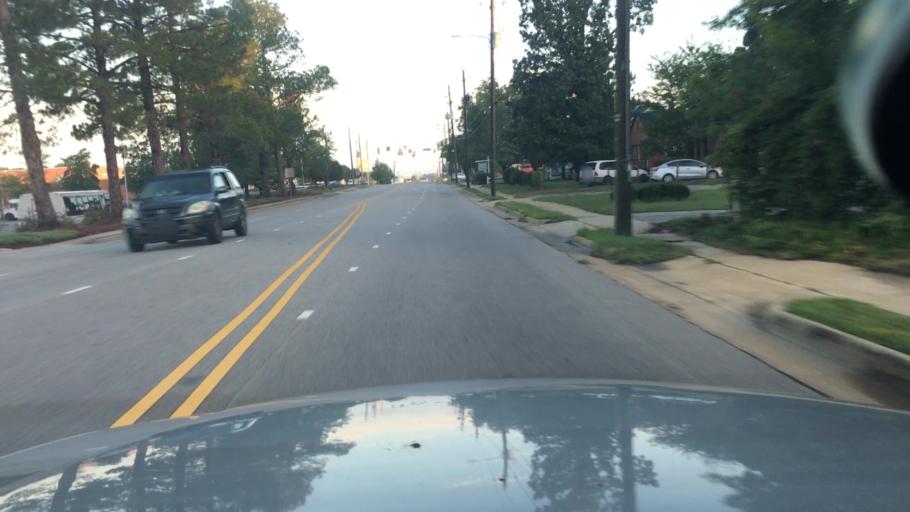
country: US
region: North Carolina
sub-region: Cumberland County
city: Fayetteville
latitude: 35.0701
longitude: -78.9224
